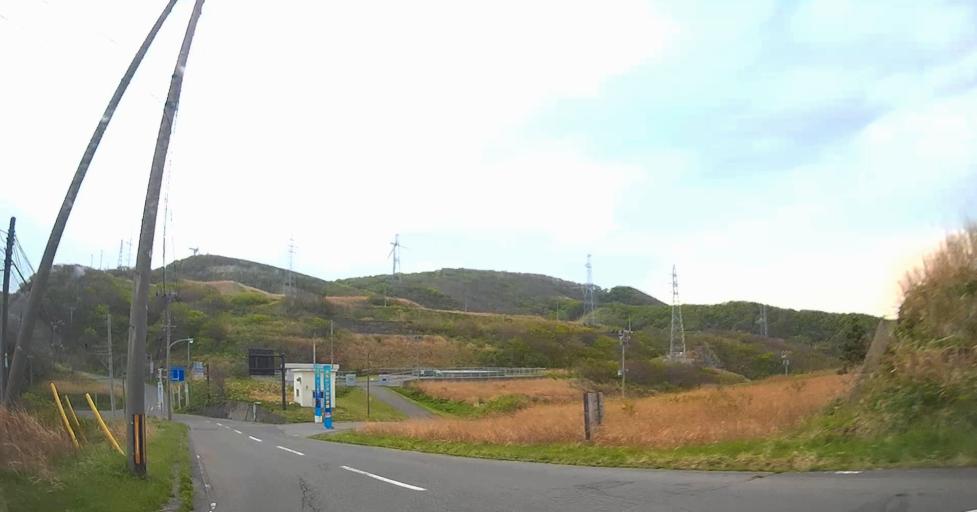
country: JP
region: Aomori
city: Shimokizukuri
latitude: 41.2549
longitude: 140.3489
